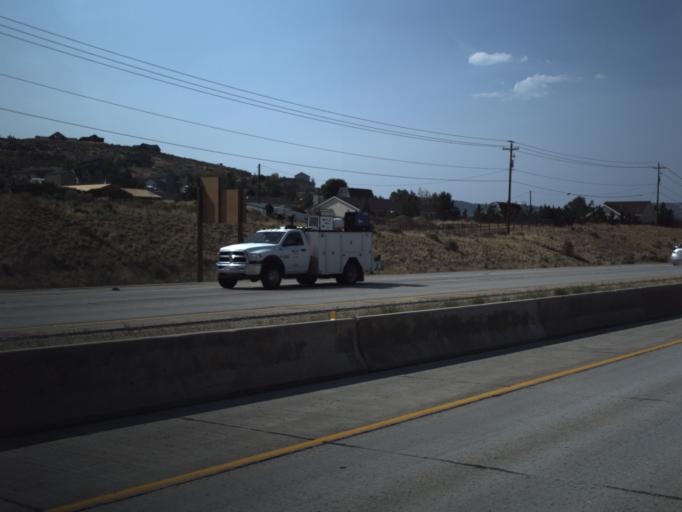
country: US
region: Utah
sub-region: Summit County
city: Snyderville
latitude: 40.7224
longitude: -111.4905
